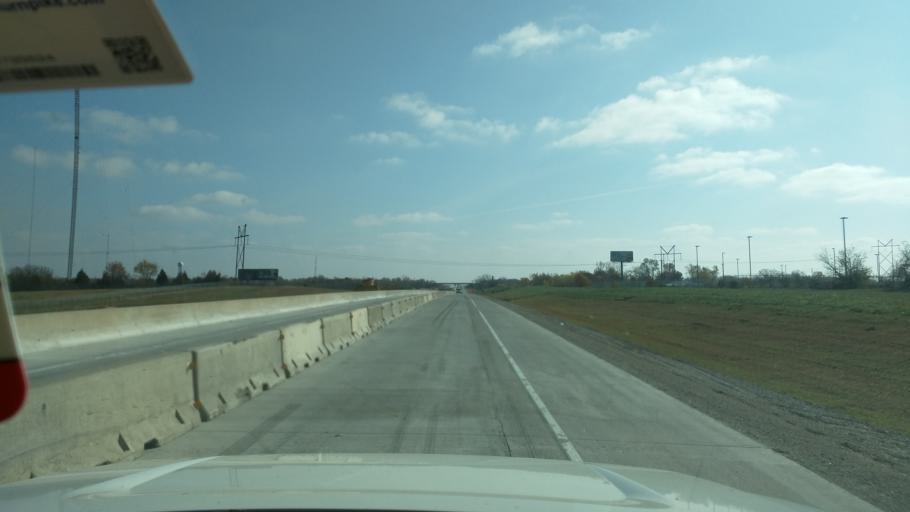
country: US
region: Oklahoma
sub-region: Wagoner County
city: Coweta
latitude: 36.0214
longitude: -95.6848
